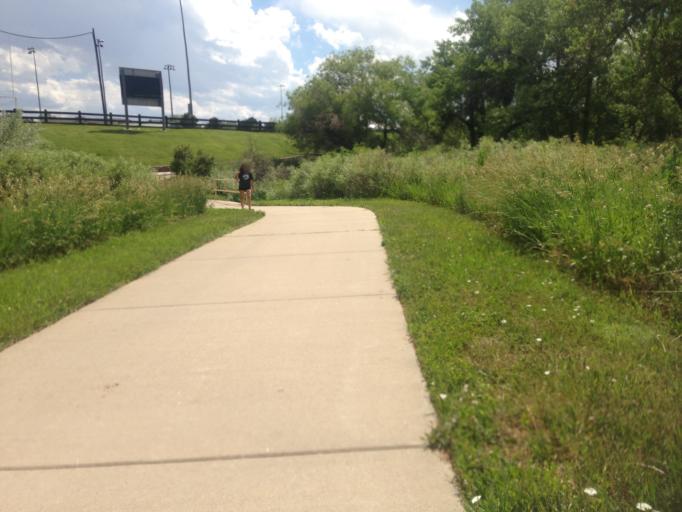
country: US
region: Colorado
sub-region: Boulder County
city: Superior
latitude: 39.9317
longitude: -105.1499
